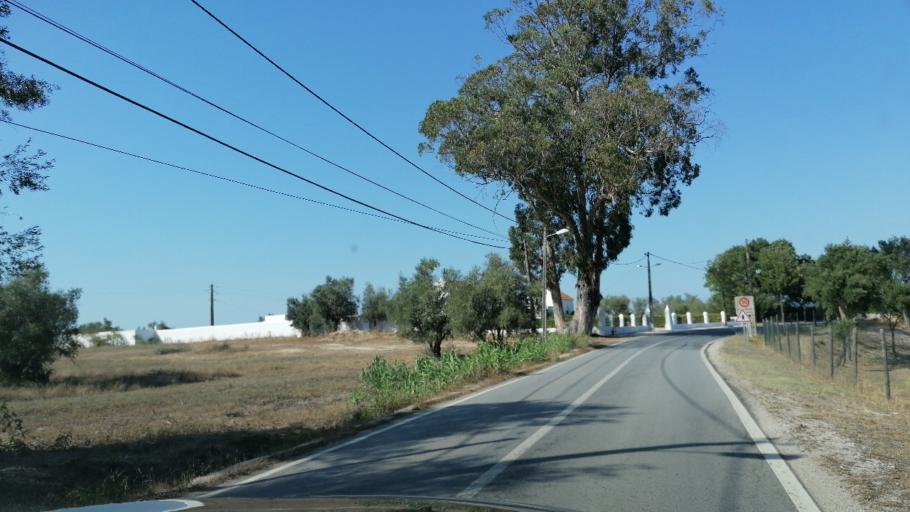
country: PT
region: Santarem
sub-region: Benavente
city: Poceirao
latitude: 38.7643
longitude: -8.6296
